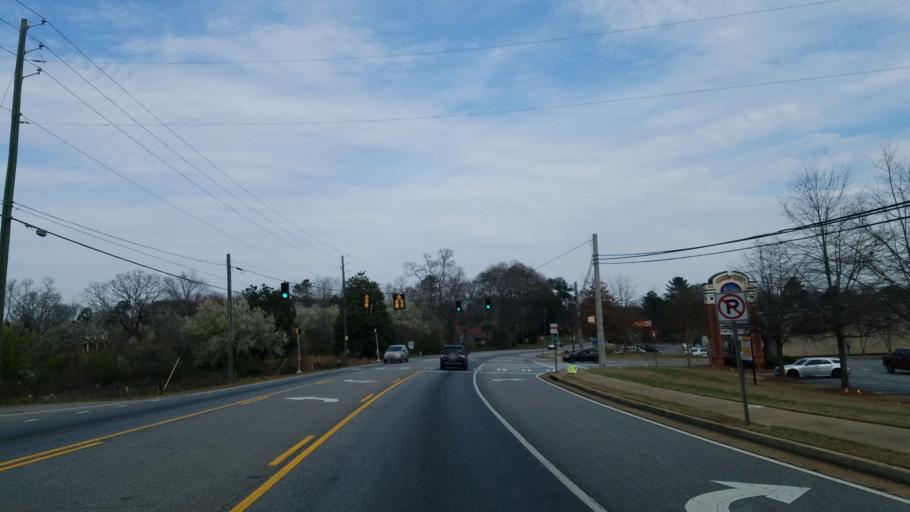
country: US
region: Georgia
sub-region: Cherokee County
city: Ball Ground
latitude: 34.2543
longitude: -84.3588
